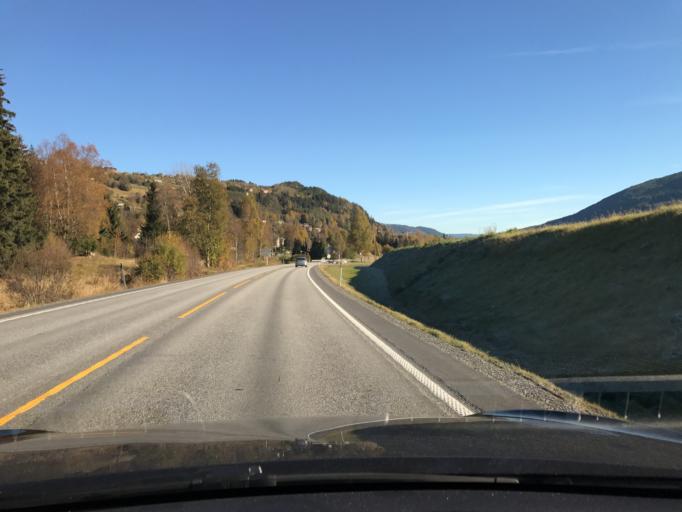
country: NO
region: Buskerud
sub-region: Al
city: Al
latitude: 60.6234
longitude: 8.5376
